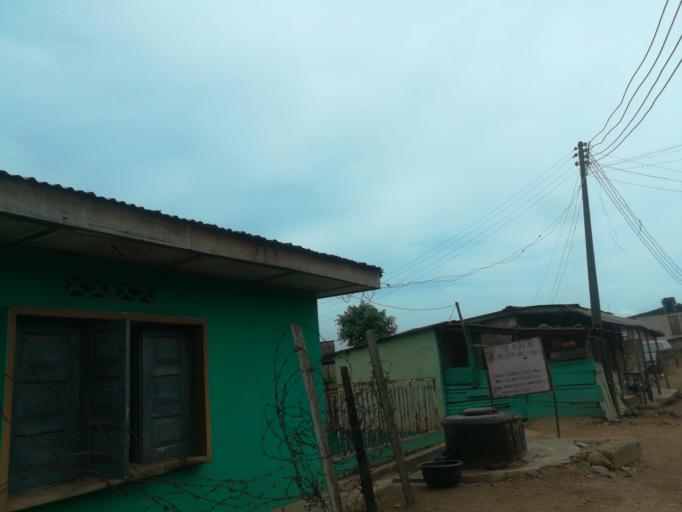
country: NG
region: Oyo
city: Ibadan
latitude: 7.3748
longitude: 3.9319
